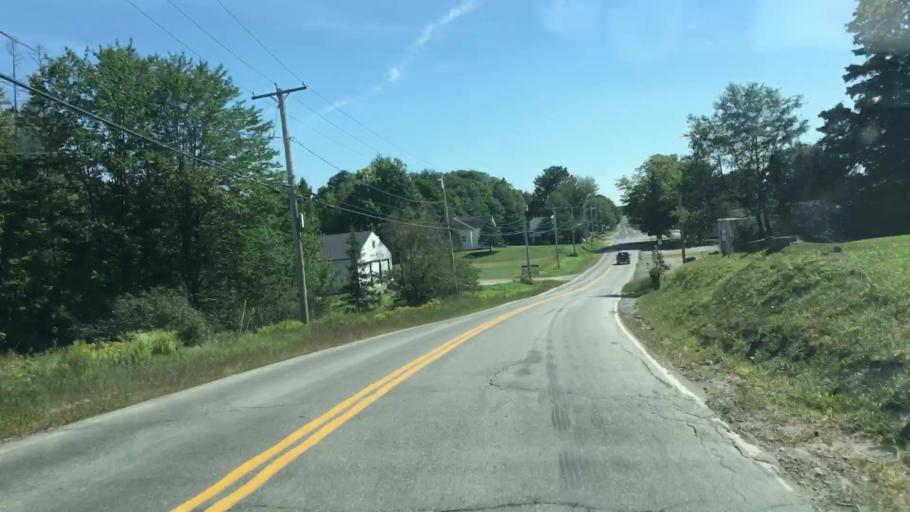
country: US
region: Maine
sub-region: Penobscot County
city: Bradford
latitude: 45.1691
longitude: -68.8470
